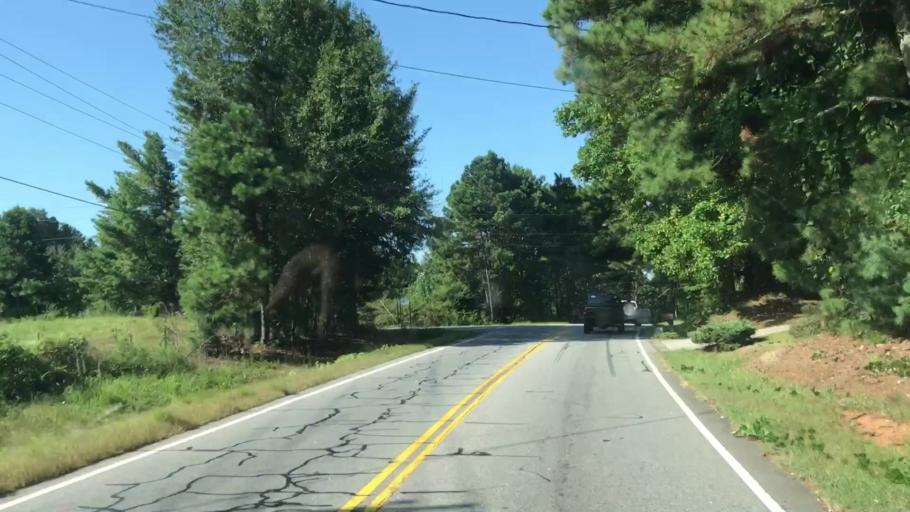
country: US
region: Georgia
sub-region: Walton County
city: Loganville
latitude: 33.8859
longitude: -83.8116
